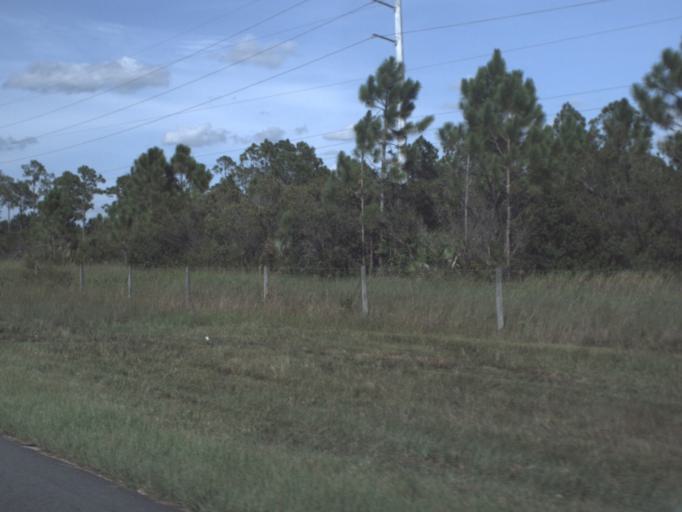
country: US
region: Florida
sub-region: Lee County
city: Olga
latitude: 26.8430
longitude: -81.7598
